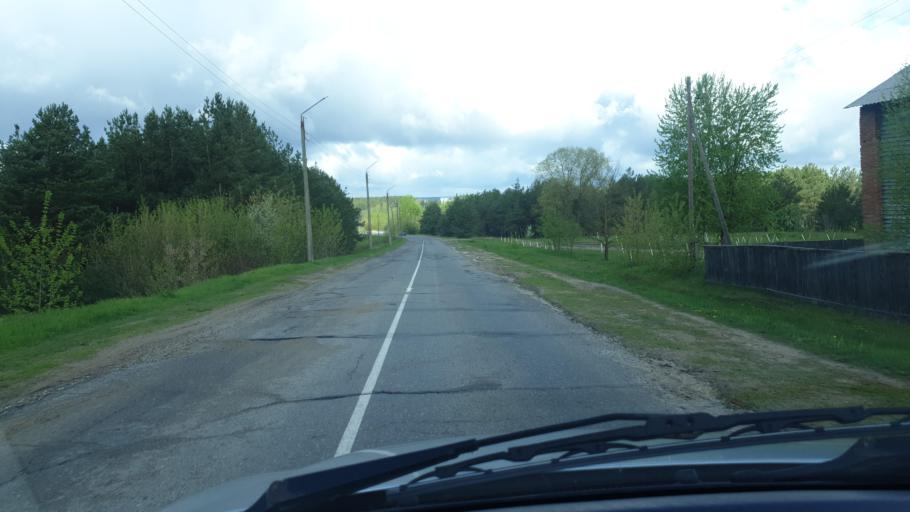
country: BY
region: Vitebsk
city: Lyepyel'
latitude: 54.8762
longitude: 28.6731
